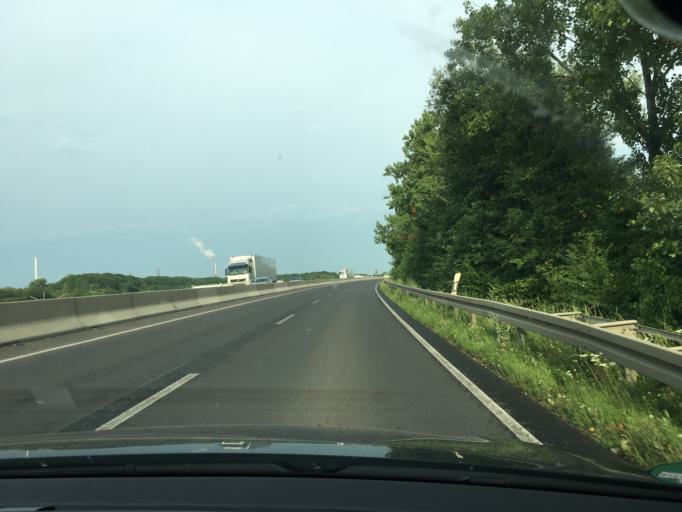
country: DE
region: North Rhine-Westphalia
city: Wesseling
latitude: 50.8505
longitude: 6.9483
